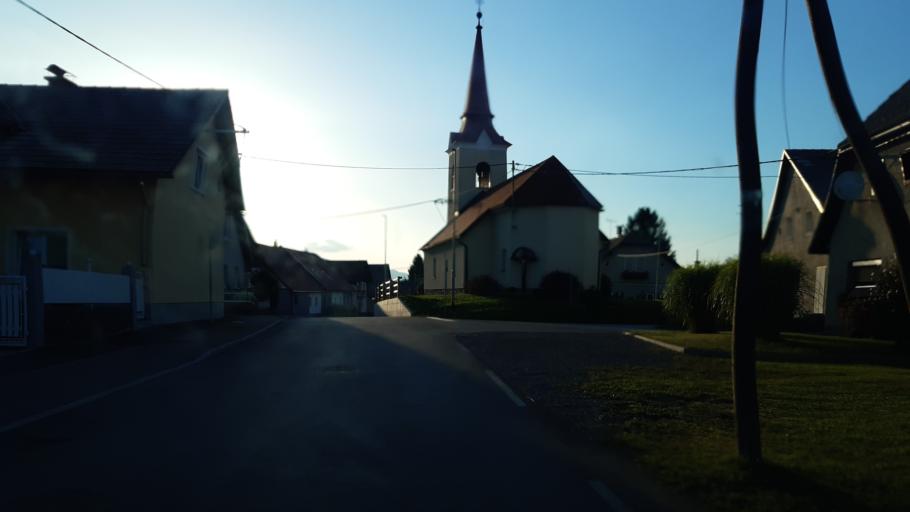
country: SI
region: Kocevje
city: Kocevje
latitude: 45.6581
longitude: 14.8858
